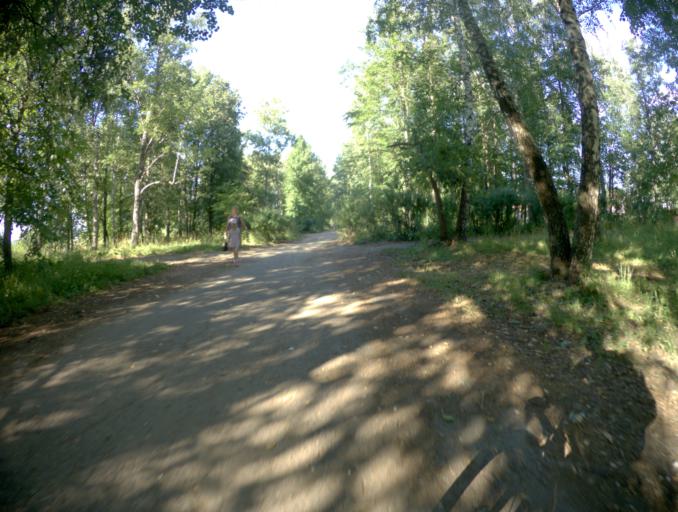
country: RU
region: Nizjnij Novgorod
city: Taremskoye
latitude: 55.9613
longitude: 43.0501
